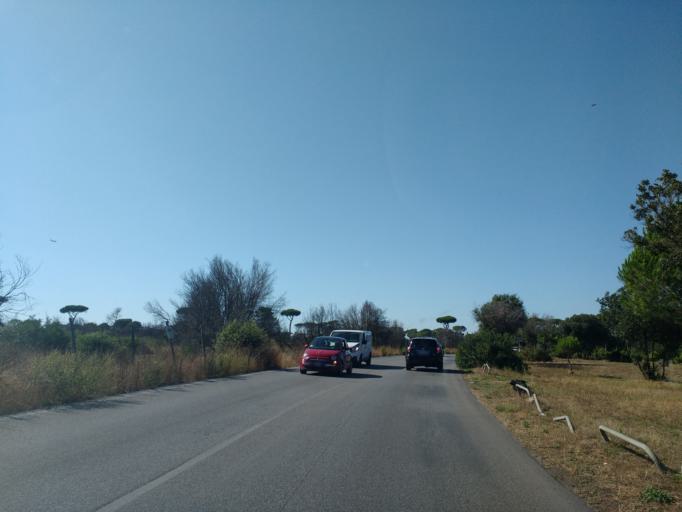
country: IT
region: Latium
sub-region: Citta metropolitana di Roma Capitale
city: Acilia-Castel Fusano-Ostia Antica
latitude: 41.7276
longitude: 12.3392
